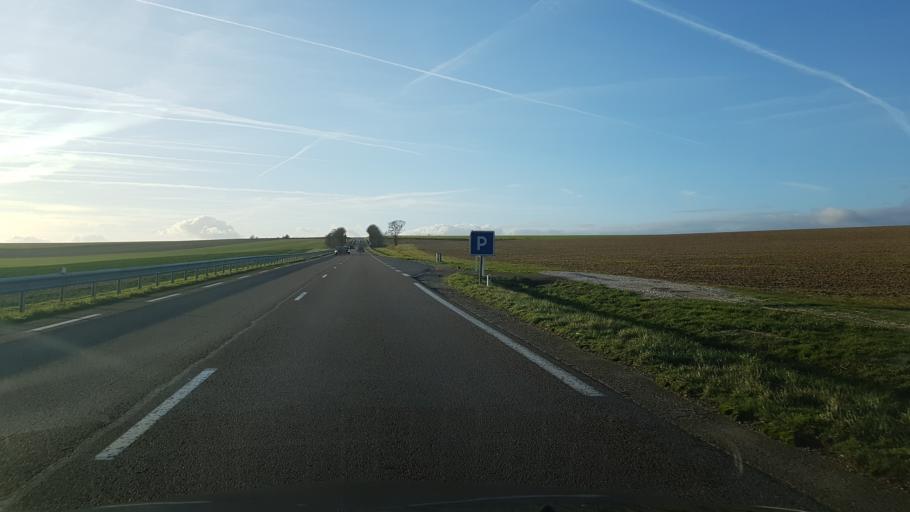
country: FR
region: Champagne-Ardenne
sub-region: Departement de l'Aube
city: Mailly-le-Camp
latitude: 48.7350
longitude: 4.2969
